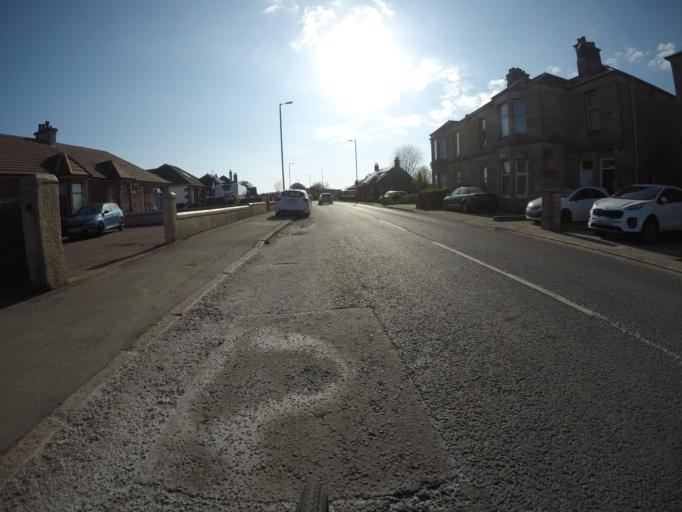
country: GB
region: Scotland
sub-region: North Ayrshire
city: Kilwinning
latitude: 55.6523
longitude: -4.7168
